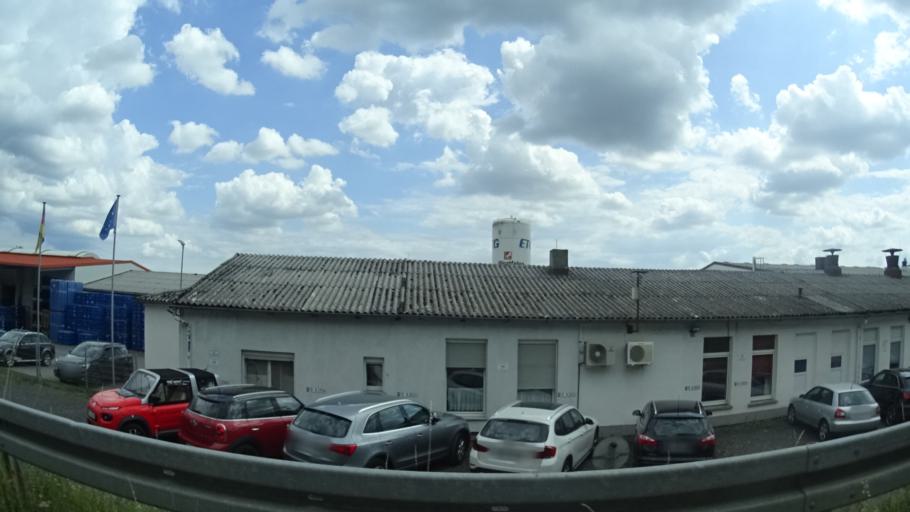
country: DE
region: Hesse
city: Gedern
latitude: 50.4173
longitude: 9.2269
